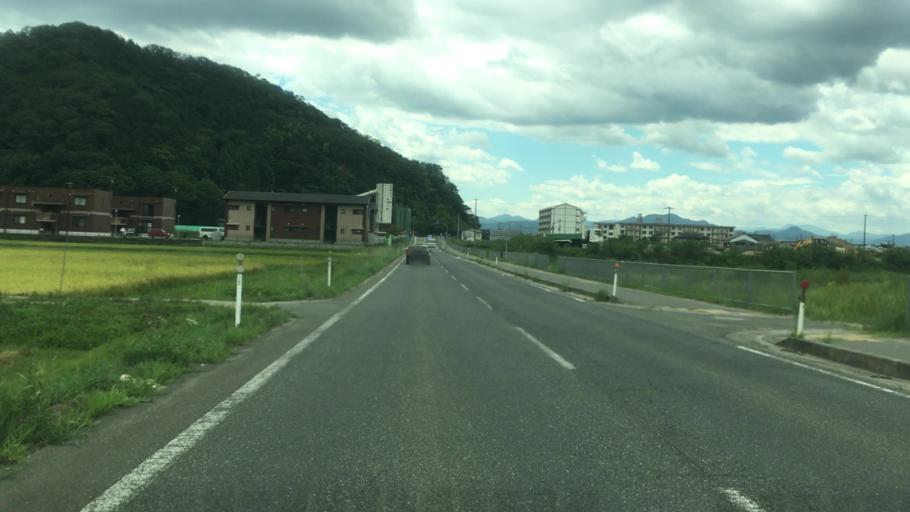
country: JP
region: Hyogo
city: Toyooka
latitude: 35.5514
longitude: 134.8424
